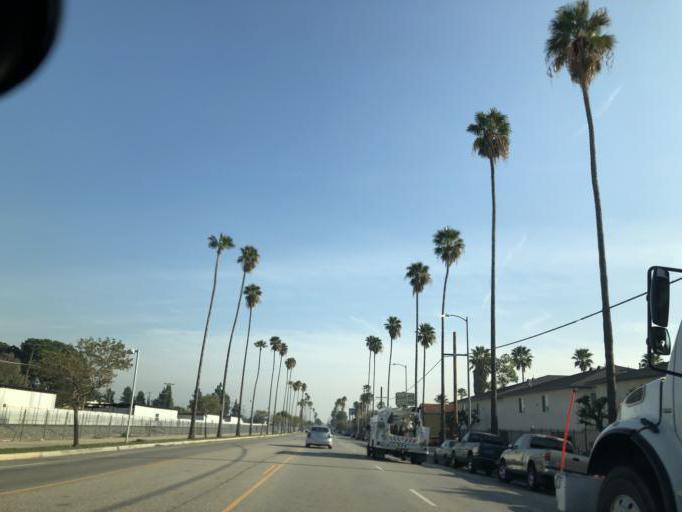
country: US
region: California
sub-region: Los Angeles County
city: San Fernando
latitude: 34.3027
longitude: -118.4639
